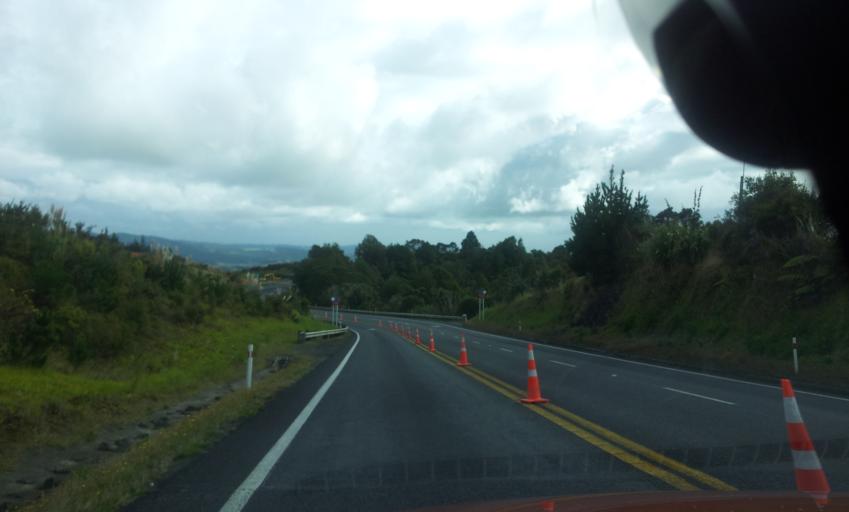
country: NZ
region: Northland
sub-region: Whangarei
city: Ruakaka
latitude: -36.0586
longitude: 174.4270
